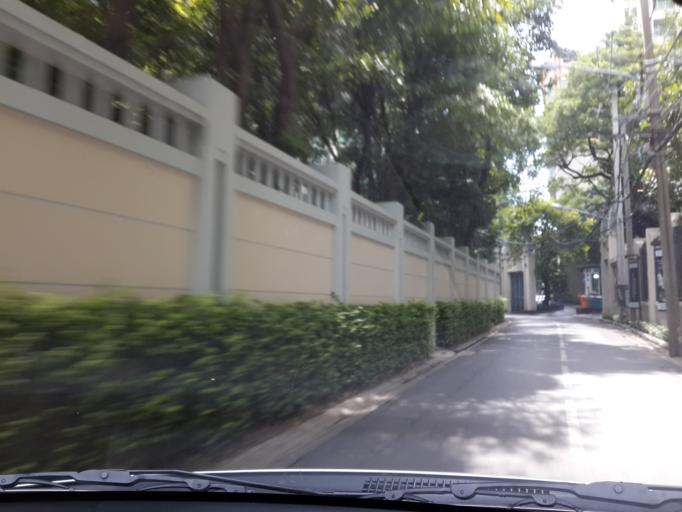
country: TH
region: Bangkok
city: Ratchathewi
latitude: 13.7478
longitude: 100.5460
